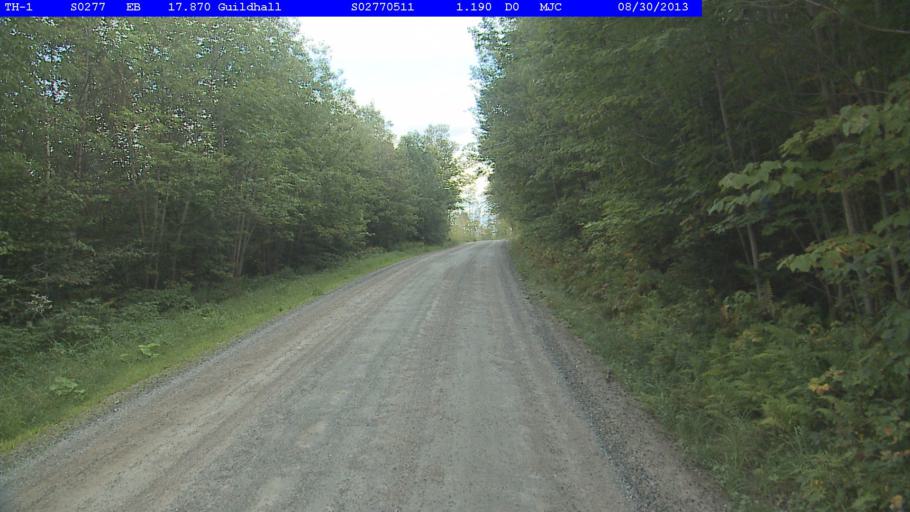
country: US
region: Vermont
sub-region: Essex County
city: Guildhall
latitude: 44.5689
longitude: -71.6474
